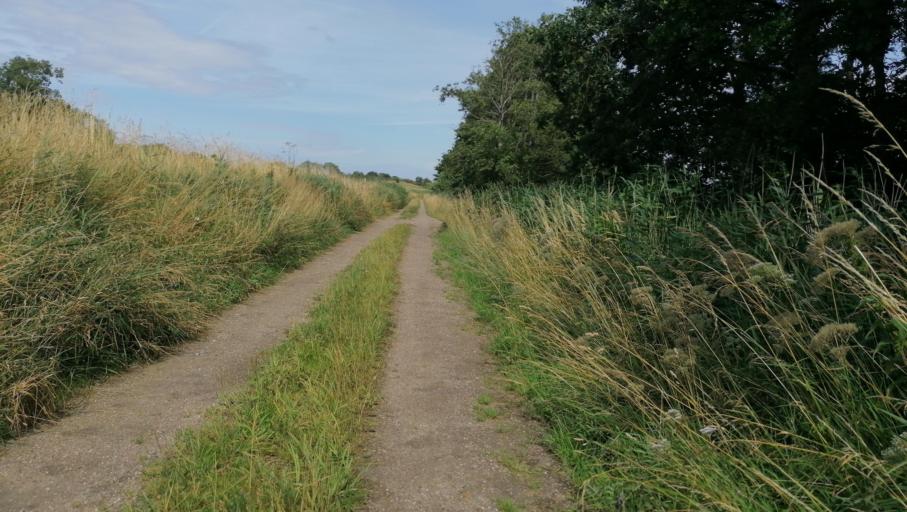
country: DK
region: Zealand
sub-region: Odsherred Kommune
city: Horve
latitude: 55.7872
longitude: 11.4220
